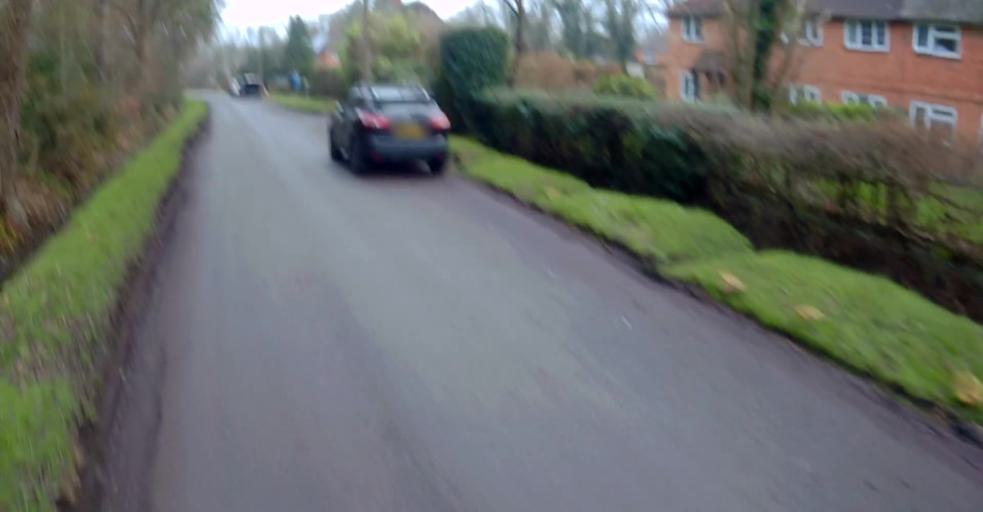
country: GB
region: England
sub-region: Hampshire
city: Eversley
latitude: 51.3537
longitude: -0.9000
